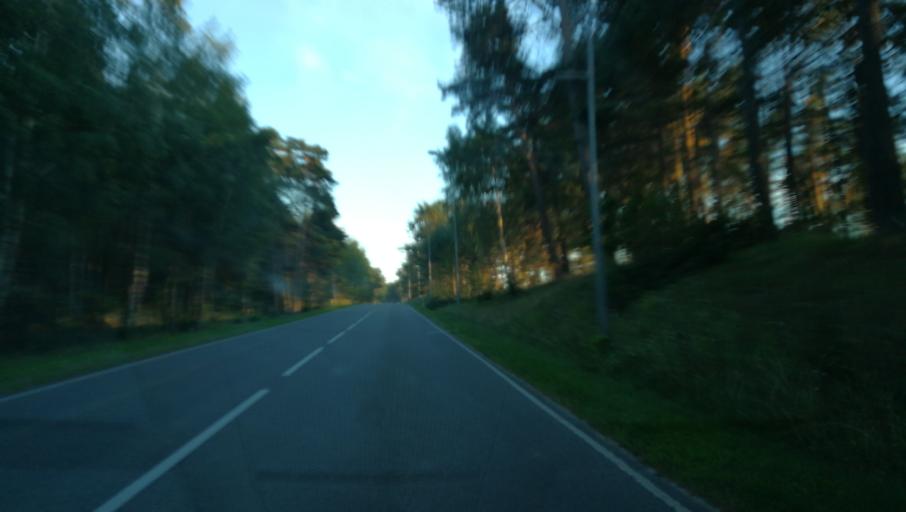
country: LV
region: Saulkrastu
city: Saulkrasti
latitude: 57.2908
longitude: 24.4114
